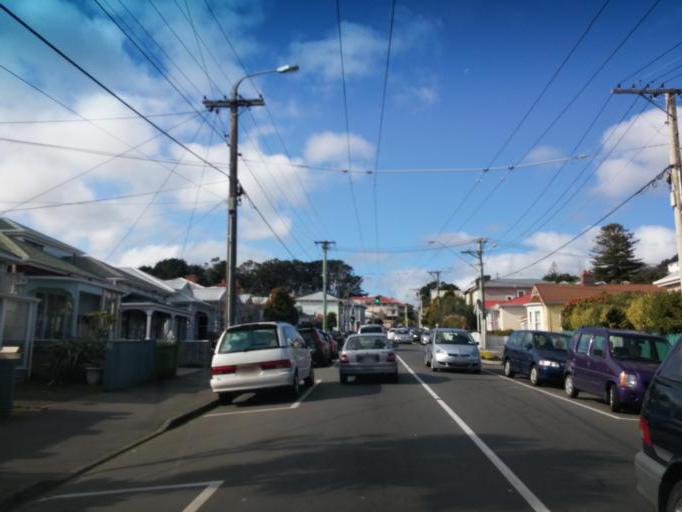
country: NZ
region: Wellington
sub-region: Wellington City
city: Wellington
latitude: -41.3129
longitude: 174.7849
